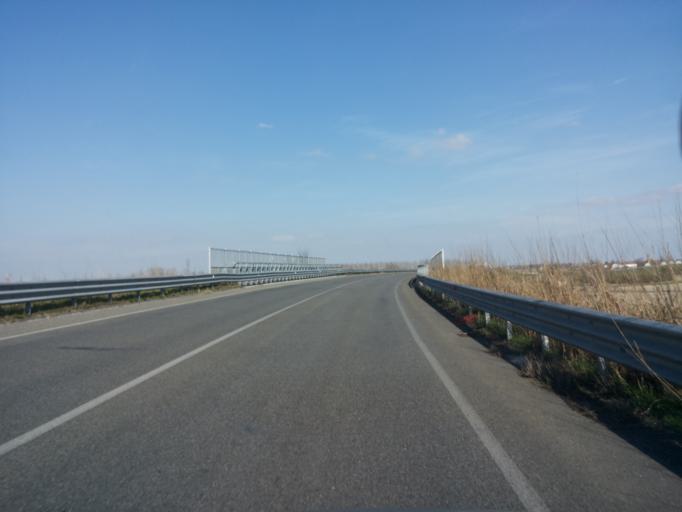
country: IT
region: Piedmont
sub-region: Provincia di Alessandria
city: Morano sul Po
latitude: 45.1726
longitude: 8.3589
